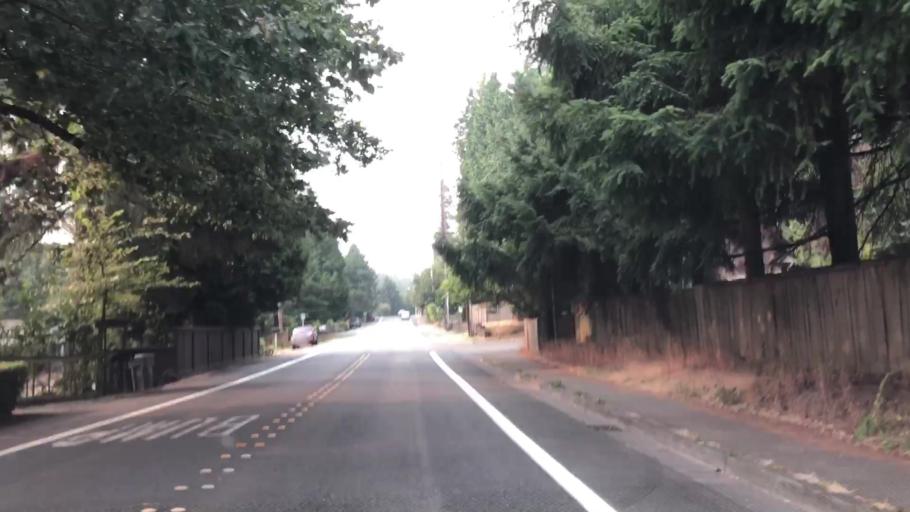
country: US
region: Washington
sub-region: King County
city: Redmond
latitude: 47.6647
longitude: -122.1352
